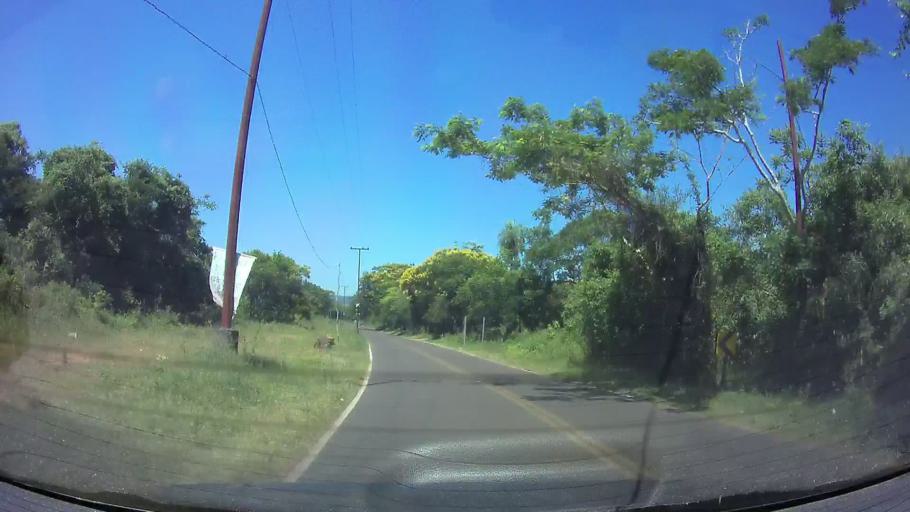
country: PY
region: Central
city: Aregua
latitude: -25.2888
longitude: -57.4062
